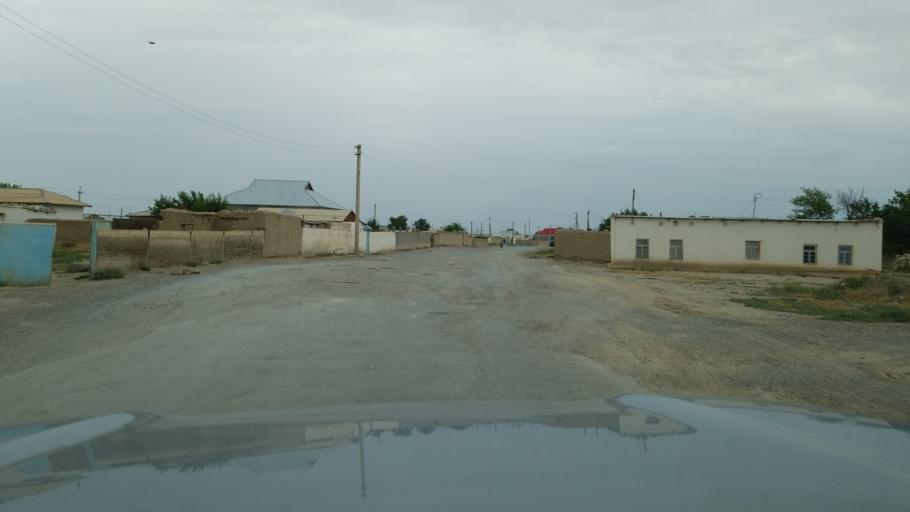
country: TM
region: Balkan
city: Serdar
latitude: 38.9894
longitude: 56.2774
